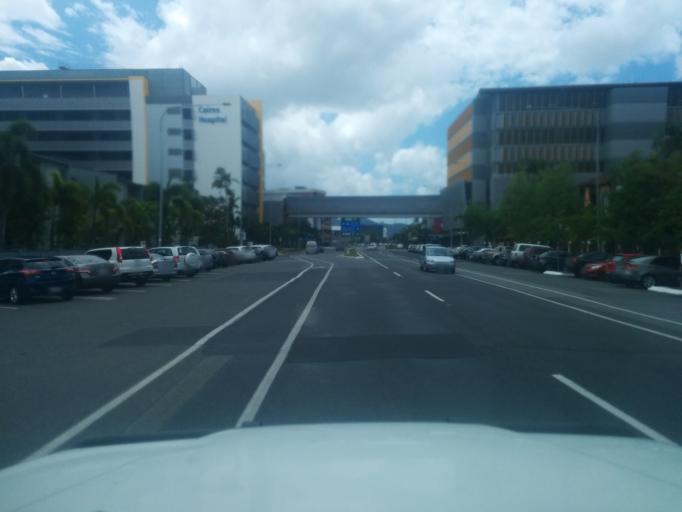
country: AU
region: Queensland
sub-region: Cairns
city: Cairns
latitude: -16.9109
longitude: 145.7660
